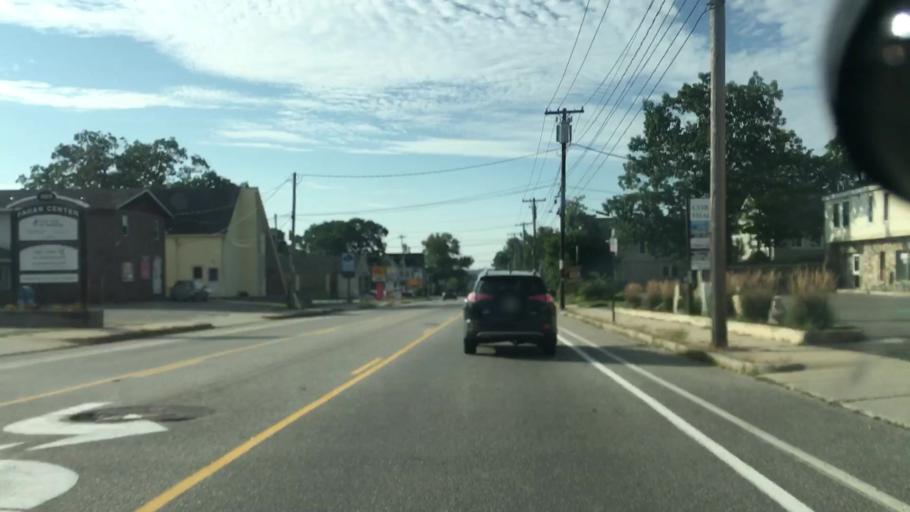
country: US
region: Maine
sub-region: Cumberland County
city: Portland
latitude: 43.6815
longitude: -70.2899
